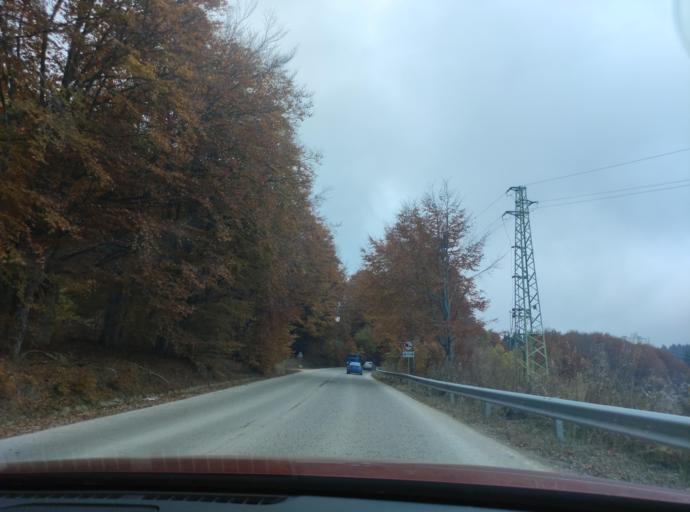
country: BG
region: Montana
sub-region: Obshtina Berkovitsa
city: Berkovitsa
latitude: 43.1194
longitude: 23.1211
